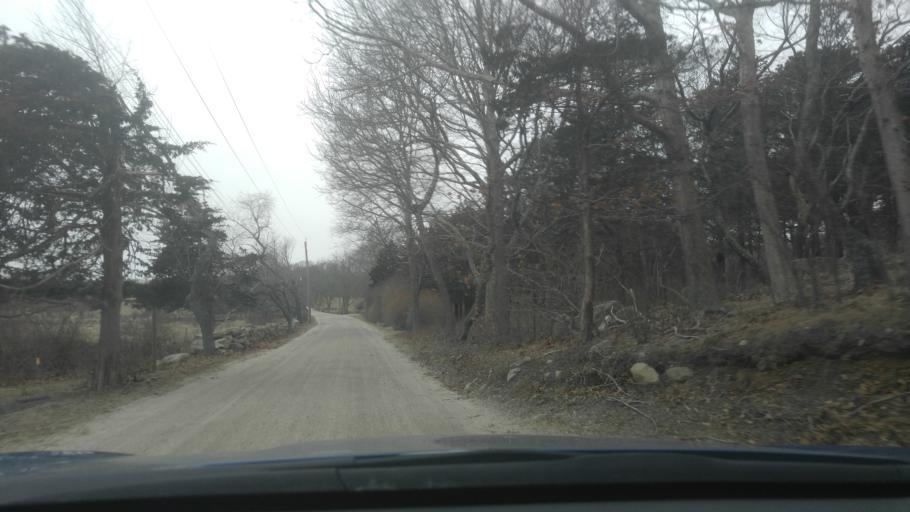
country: US
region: Rhode Island
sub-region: Washington County
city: Wakefield-Peacedale
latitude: 41.4086
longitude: -71.5214
